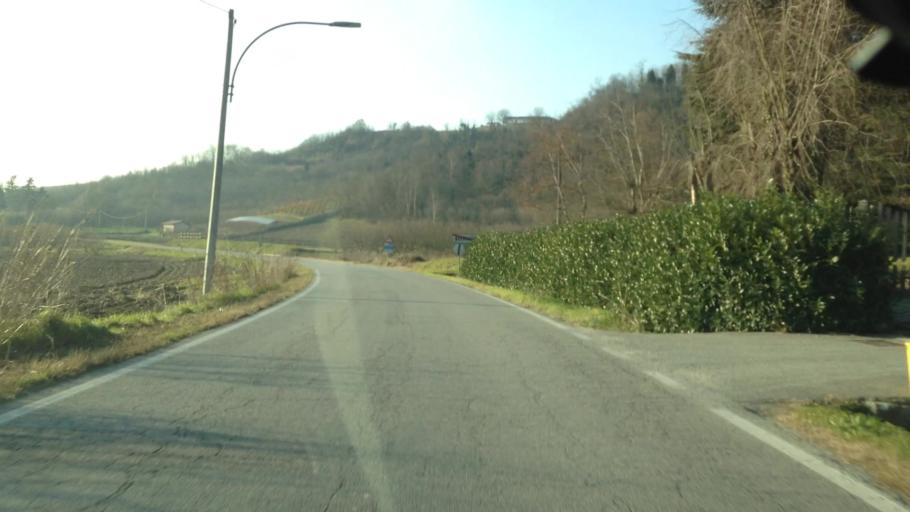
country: IT
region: Piedmont
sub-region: Provincia di Asti
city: Belveglio
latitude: 44.8306
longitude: 8.3219
